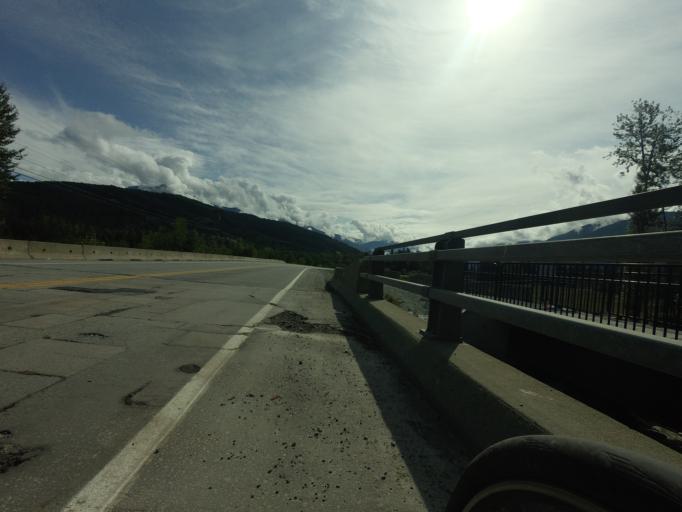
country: CA
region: British Columbia
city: Pemberton
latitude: 50.3163
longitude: -122.7674
